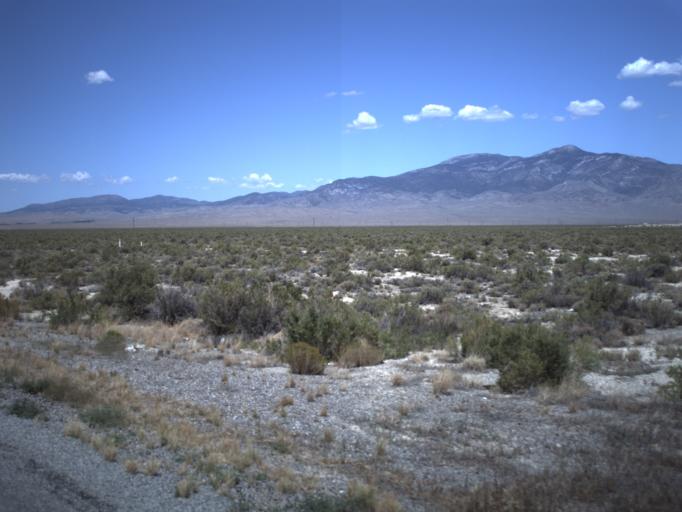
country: US
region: Nevada
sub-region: White Pine County
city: McGill
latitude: 39.0558
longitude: -114.0314
